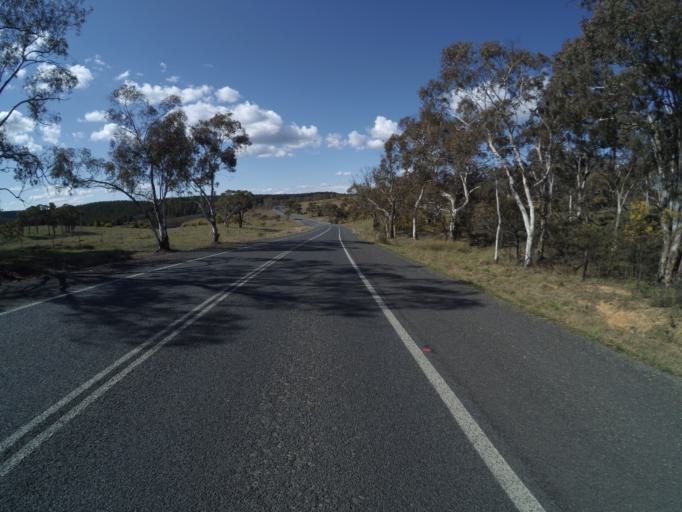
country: AU
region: New South Wales
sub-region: Queanbeyan
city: Queanbeyan
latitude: -35.3407
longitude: 149.2844
